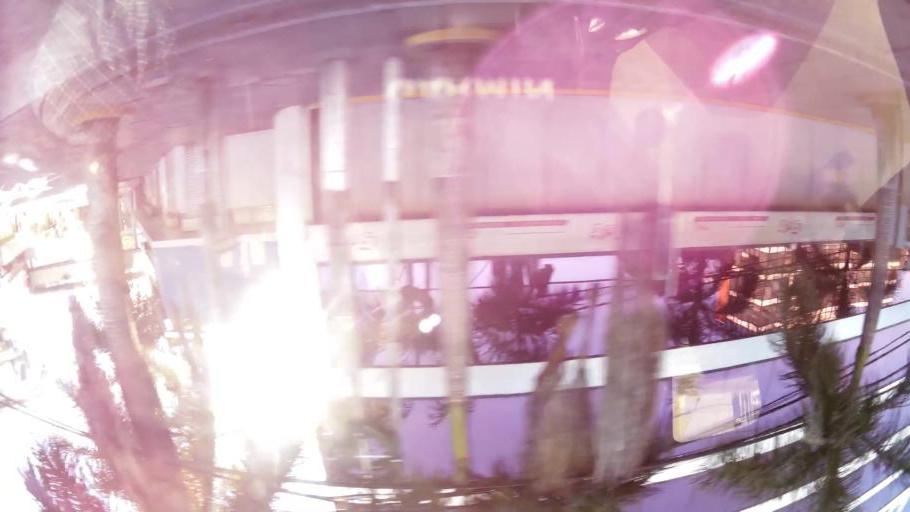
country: GT
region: Guatemala
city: Guatemala City
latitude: 14.6227
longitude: -90.5165
